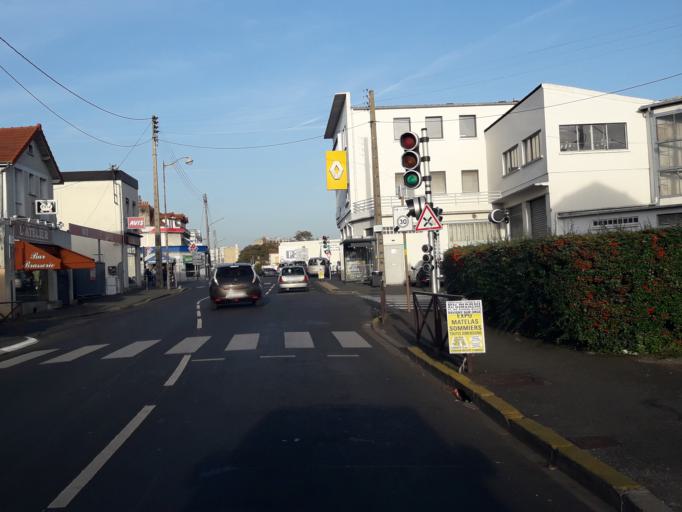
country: FR
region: Ile-de-France
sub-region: Departement de l'Essonne
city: Juvisy-sur-Orge
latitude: 48.6810
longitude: 2.3781
